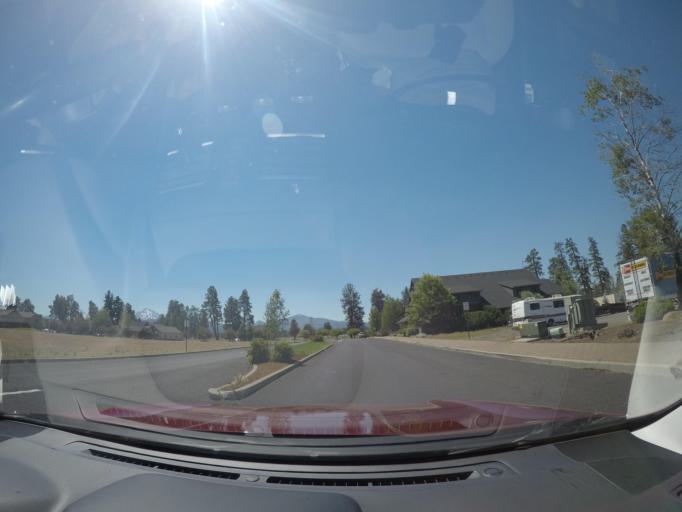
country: US
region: Oregon
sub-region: Deschutes County
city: Sisters
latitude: 44.2906
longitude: -121.5566
